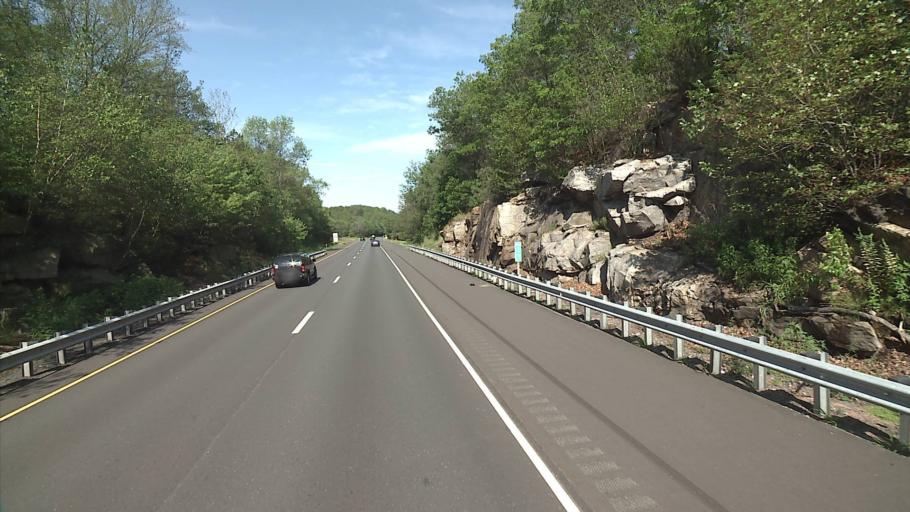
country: US
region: Connecticut
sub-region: Hartford County
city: Terramuggus
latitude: 41.6593
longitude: -72.5119
